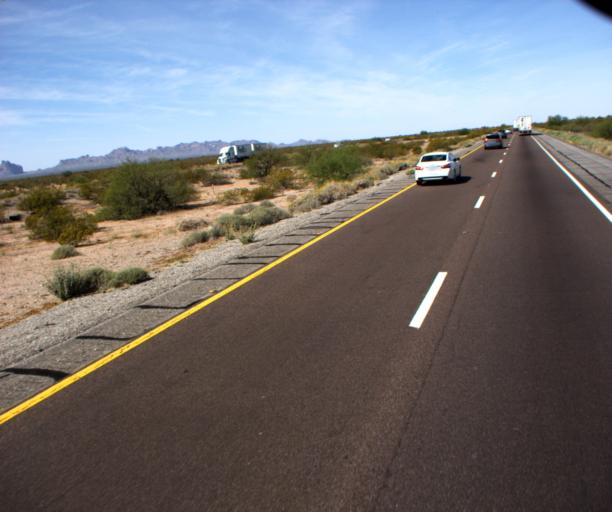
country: US
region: Arizona
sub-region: La Paz County
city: Salome
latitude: 33.5491
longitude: -113.2203
